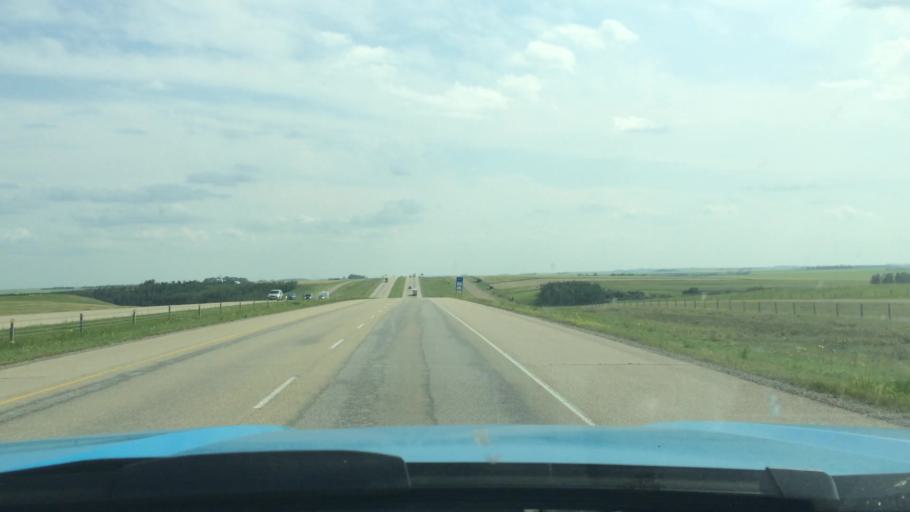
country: CA
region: Alberta
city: Carstairs
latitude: 51.5825
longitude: -114.0253
